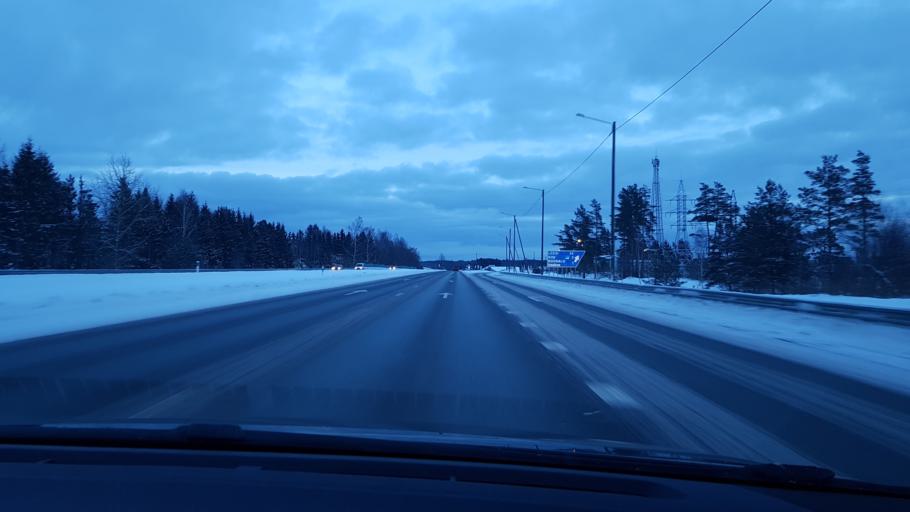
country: EE
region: Harju
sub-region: Kuusalu vald
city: Kuusalu
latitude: 59.4477
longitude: 25.4221
